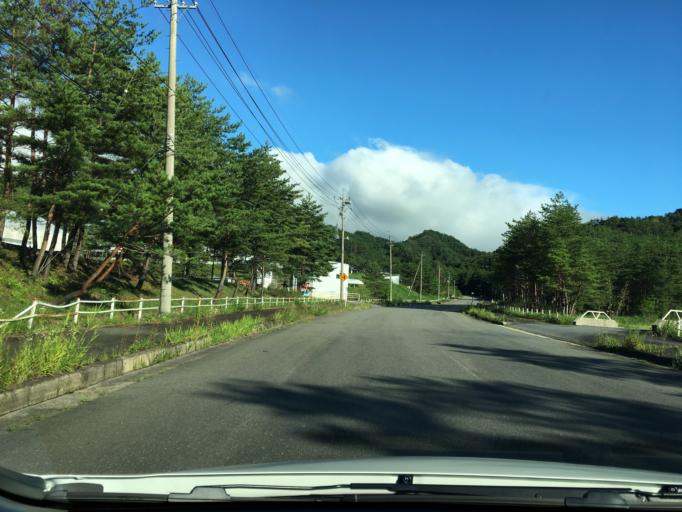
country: JP
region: Yamagata
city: Yonezawa
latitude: 37.9073
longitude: 140.1835
